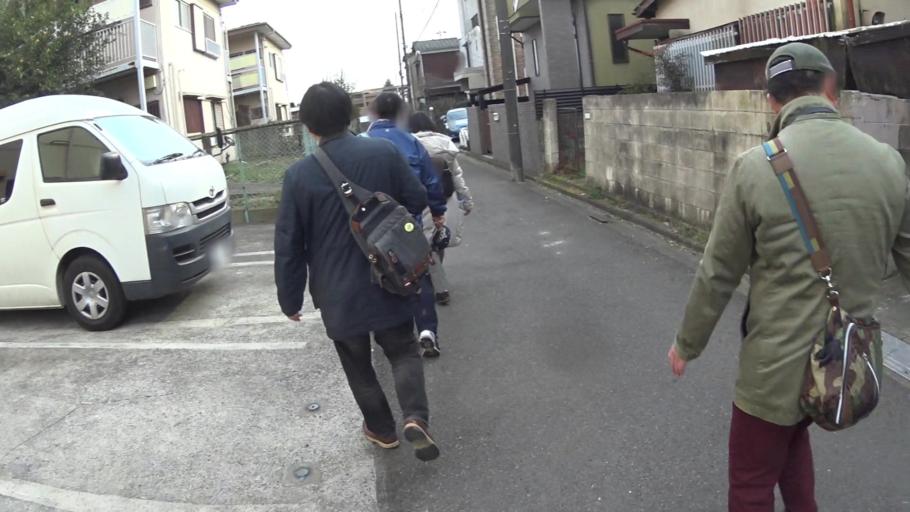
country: JP
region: Tokyo
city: Mitaka-shi
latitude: 35.6802
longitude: 139.5880
